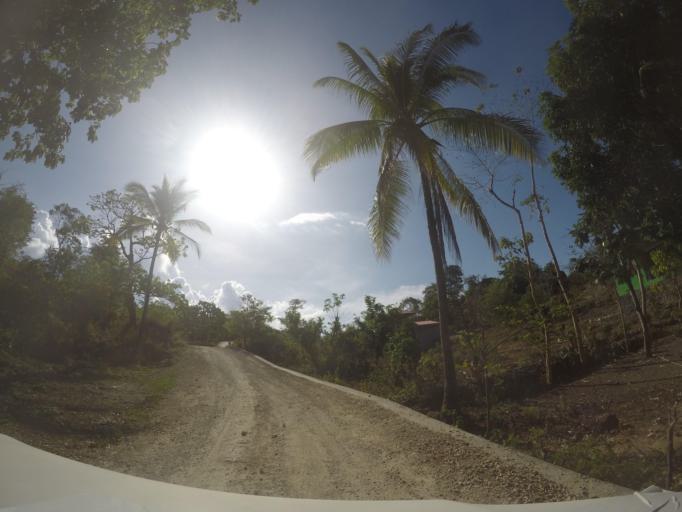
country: TL
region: Baucau
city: Baucau
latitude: -8.4549
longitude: 126.4448
